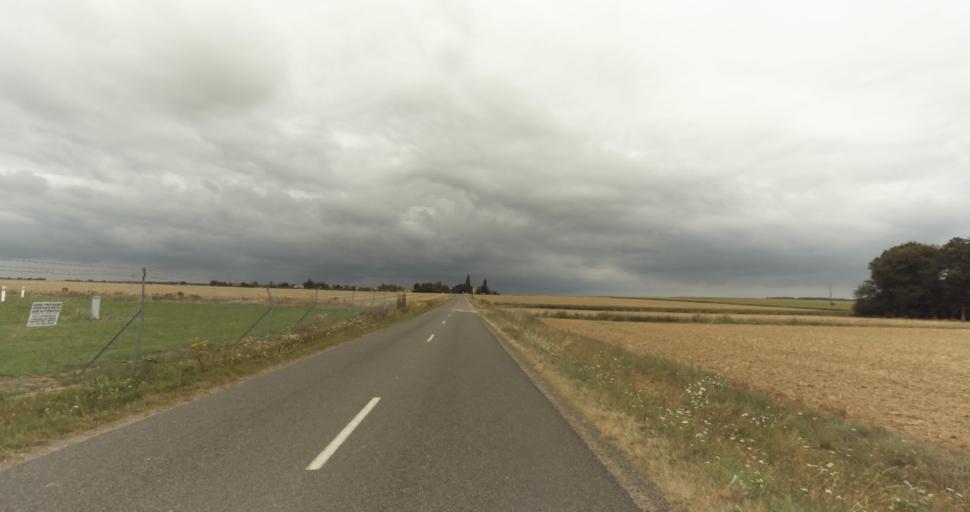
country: FR
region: Haute-Normandie
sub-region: Departement de l'Eure
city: Gravigny
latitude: 49.0462
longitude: 1.2309
